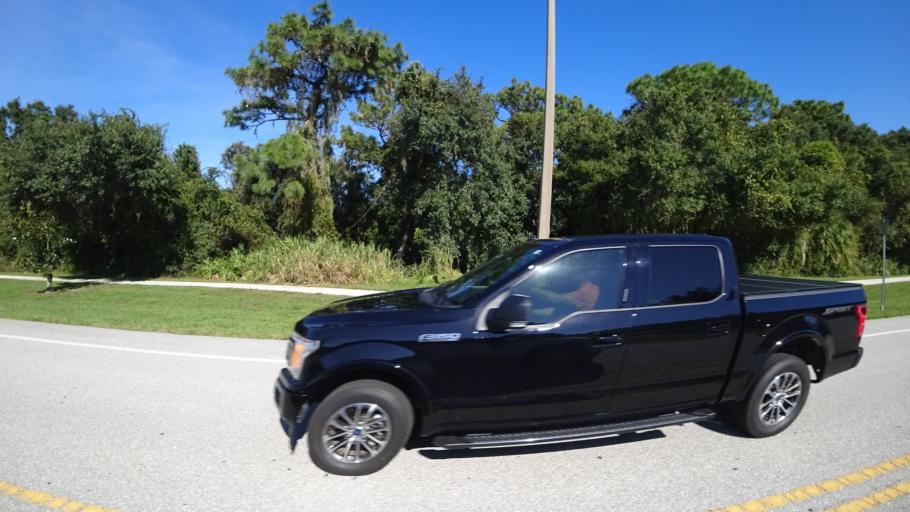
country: US
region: Florida
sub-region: Sarasota County
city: The Meadows
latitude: 27.4244
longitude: -82.4337
